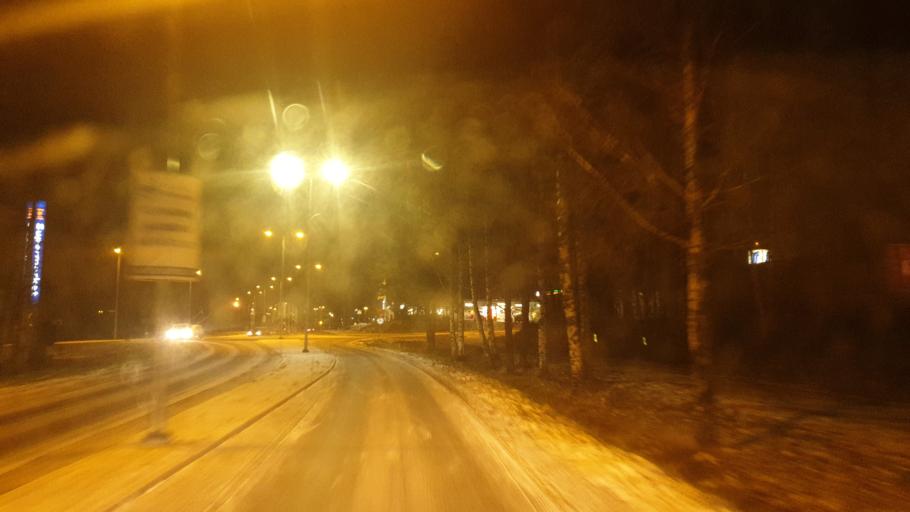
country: FI
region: Southern Savonia
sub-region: Savonlinna
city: Savonlinna
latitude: 61.8648
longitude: 28.9430
